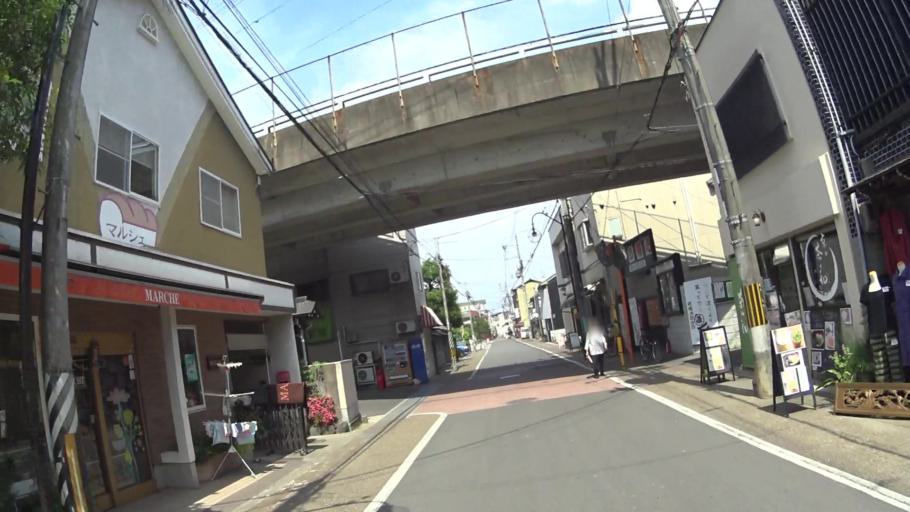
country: JP
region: Kyoto
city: Muko
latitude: 35.0162
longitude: 135.6789
